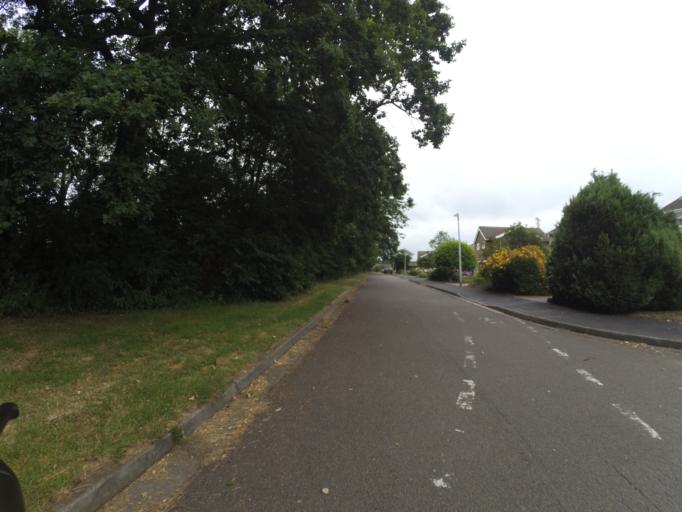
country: GB
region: England
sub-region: Warwickshire
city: Rugby
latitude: 52.3521
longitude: -1.2736
